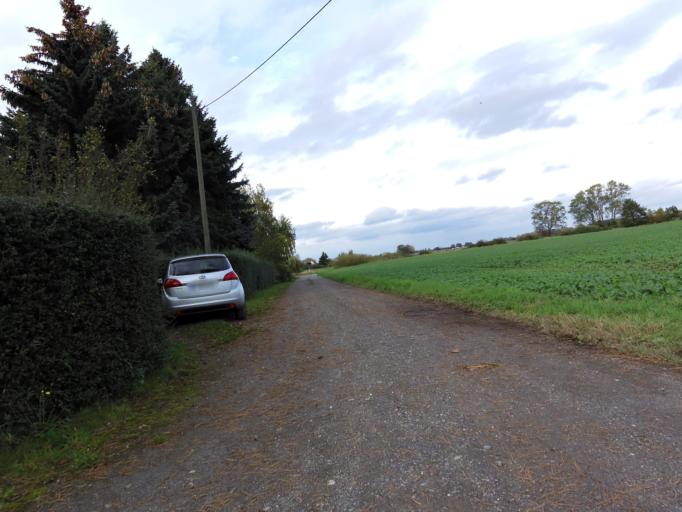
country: DE
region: Saxony
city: Grossposna
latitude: 51.2943
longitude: 12.4762
